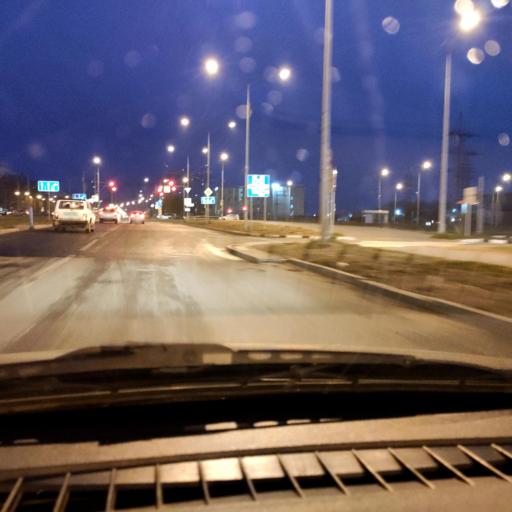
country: RU
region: Samara
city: Samara
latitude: 53.2604
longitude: 50.2407
